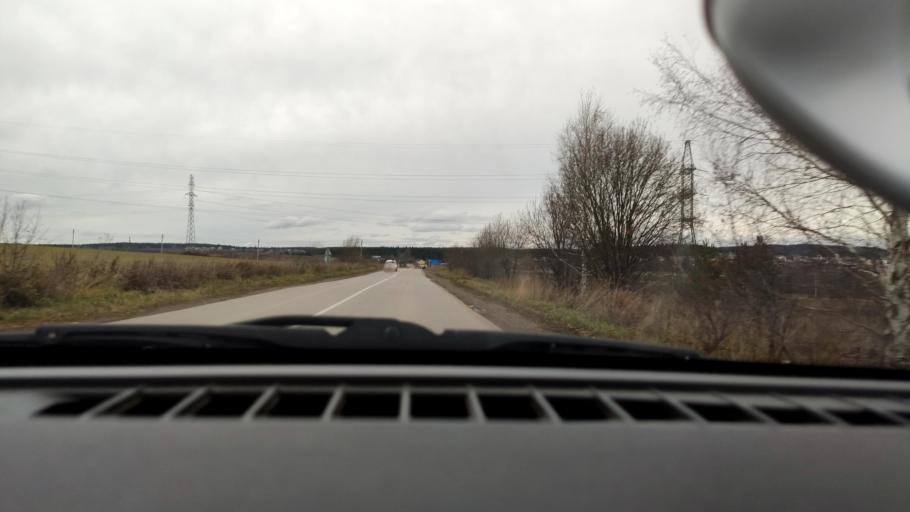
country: RU
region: Perm
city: Ferma
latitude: 57.9274
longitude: 56.3323
